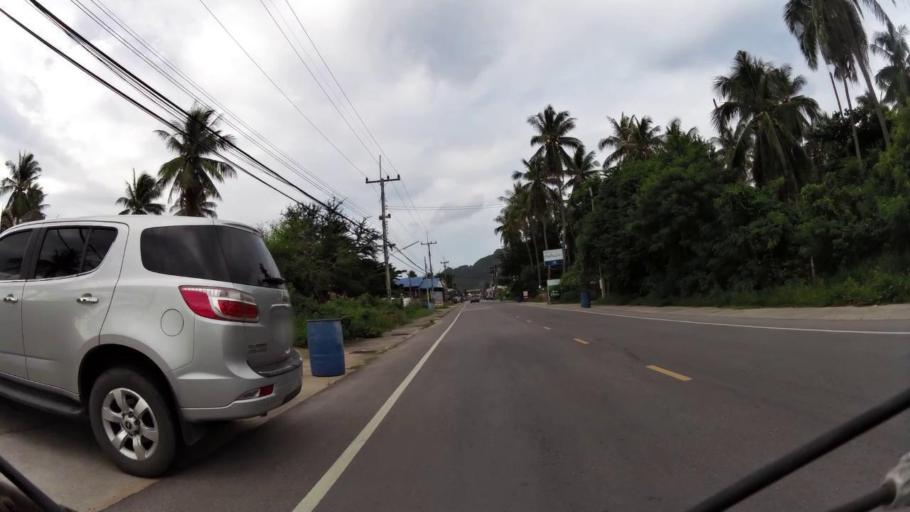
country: TH
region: Prachuap Khiri Khan
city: Prachuap Khiri Khan
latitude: 11.7367
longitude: 99.7789
